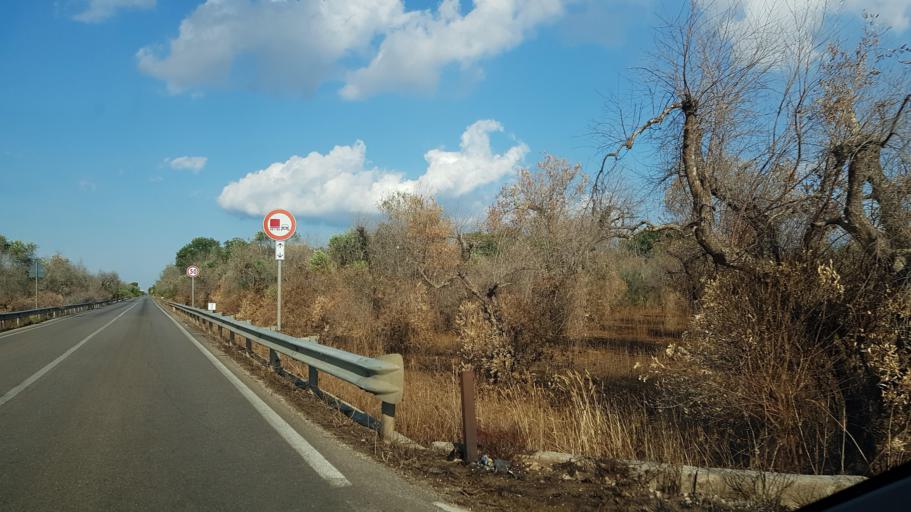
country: IT
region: Apulia
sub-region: Provincia di Lecce
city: Miggiano
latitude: 39.9637
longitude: 18.2881
